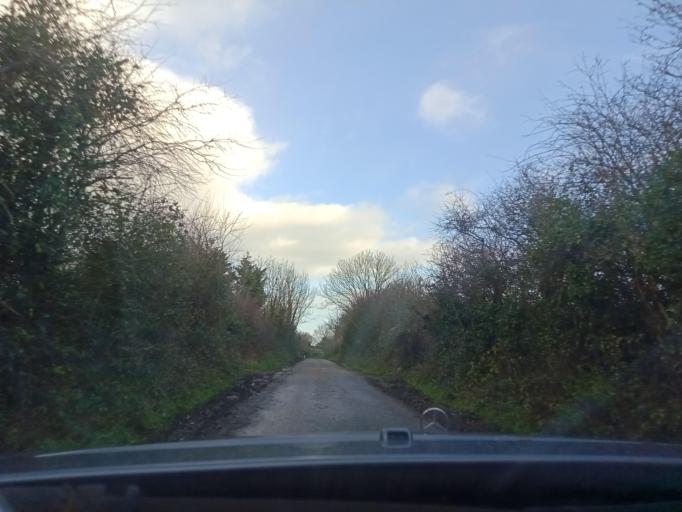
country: IE
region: Leinster
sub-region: Kilkenny
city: Callan
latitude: 52.4762
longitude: -7.3799
